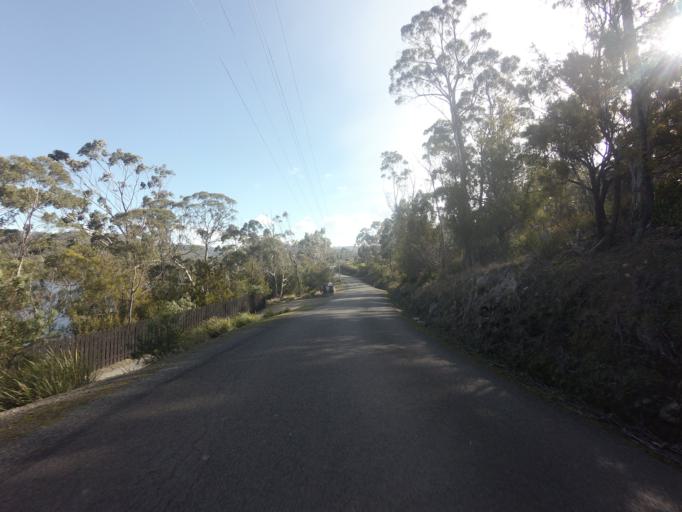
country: AU
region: Tasmania
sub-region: Kingborough
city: Kettering
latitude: -43.1217
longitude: 147.2548
